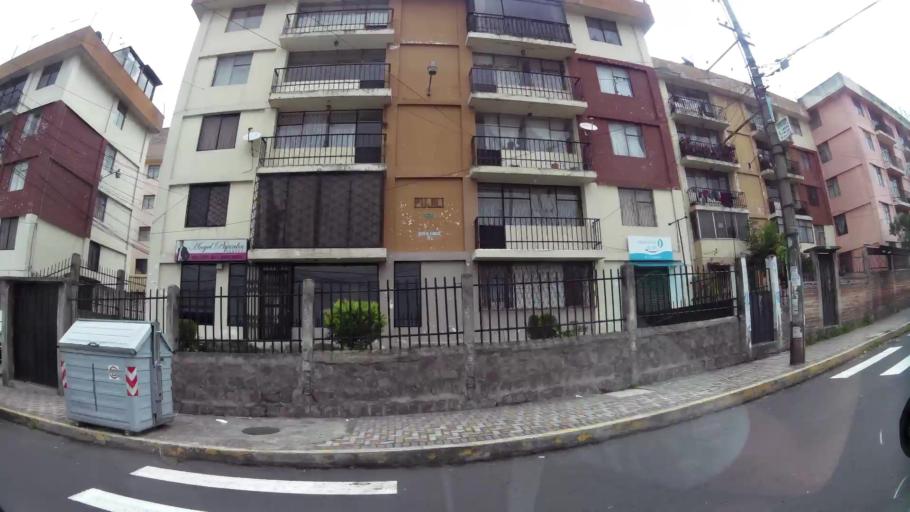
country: EC
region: Pichincha
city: Quito
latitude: -0.1258
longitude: -78.5021
